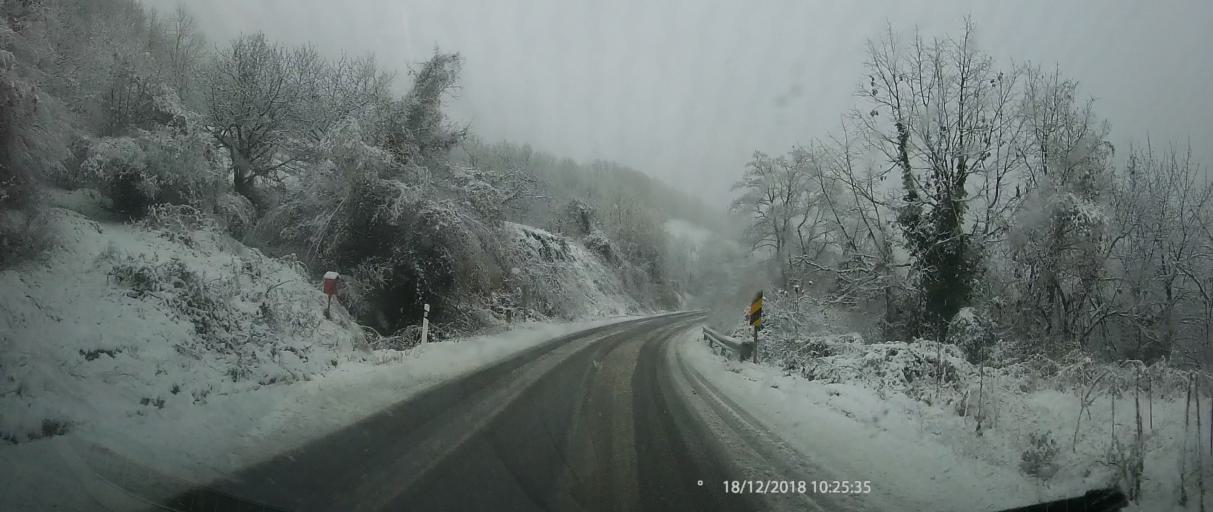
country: GR
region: Thessaly
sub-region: Nomos Larisis
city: Livadi
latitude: 40.1662
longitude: 22.2480
